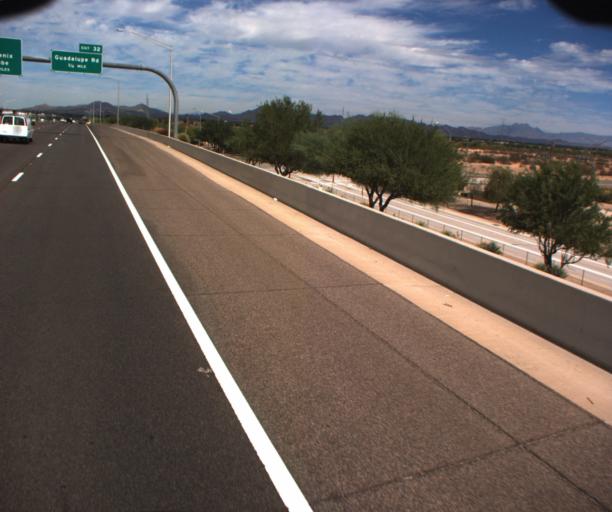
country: US
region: Arizona
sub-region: Maricopa County
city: Queen Creek
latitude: 33.3490
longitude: -111.6437
